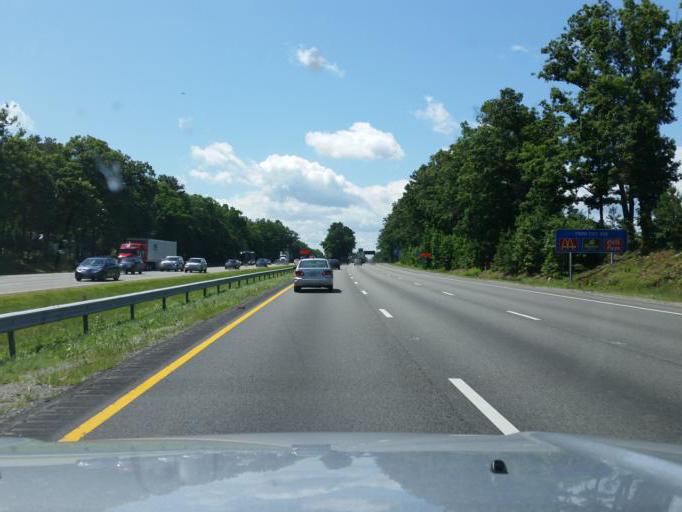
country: US
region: Virginia
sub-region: Hanover County
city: Ashland
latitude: 37.7146
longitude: -77.4480
